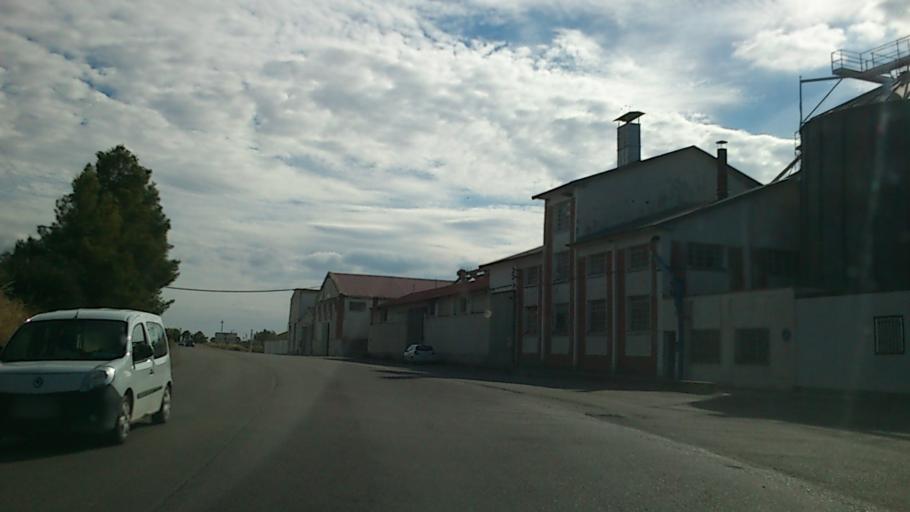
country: ES
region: Aragon
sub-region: Provincia de Zaragoza
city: San Mateo de Gallego
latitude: 41.8247
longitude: -0.7741
